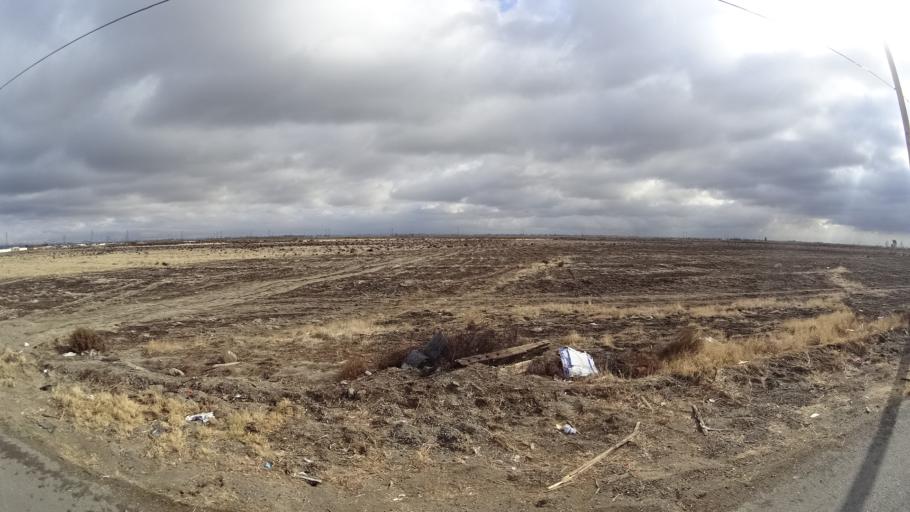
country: US
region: California
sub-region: Kern County
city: Greenfield
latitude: 35.3078
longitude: -118.9854
